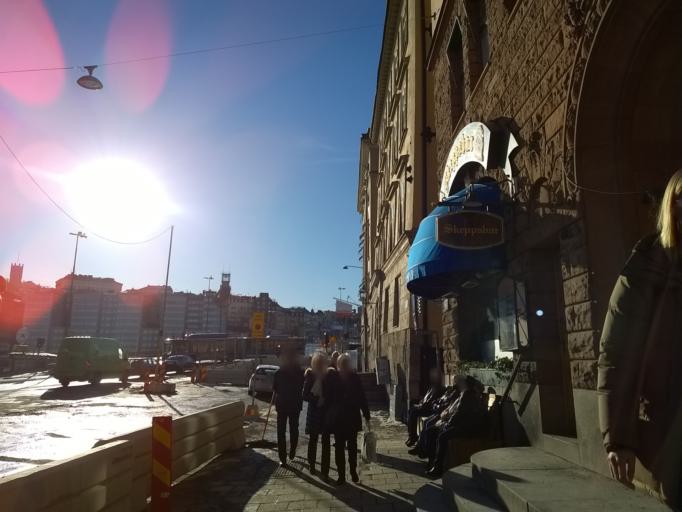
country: SE
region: Stockholm
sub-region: Stockholms Kommun
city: Stockholm
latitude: 59.3223
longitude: 18.0743
